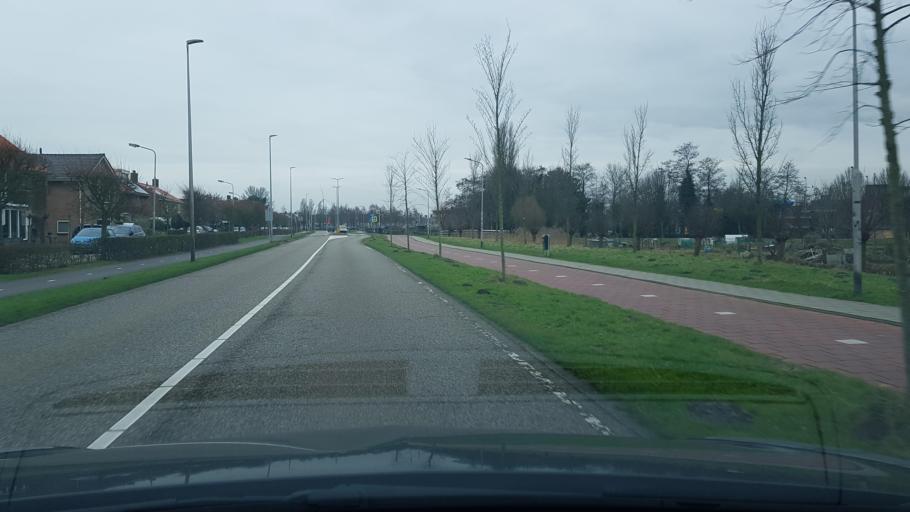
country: NL
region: North Holland
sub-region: Gemeente Uitgeest
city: Uitgeest
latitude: 52.5249
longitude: 4.7049
